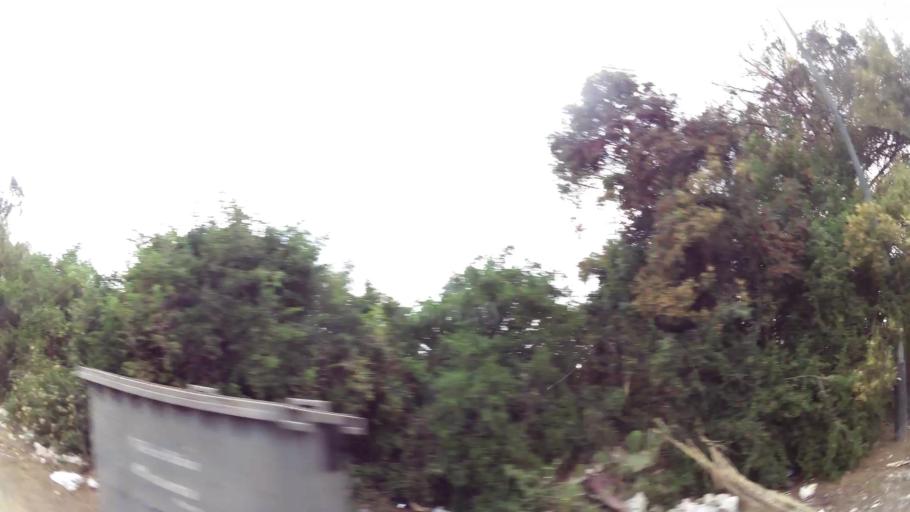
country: MA
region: Rabat-Sale-Zemmour-Zaer
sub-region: Skhirate-Temara
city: Temara
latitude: 33.9493
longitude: -6.8486
